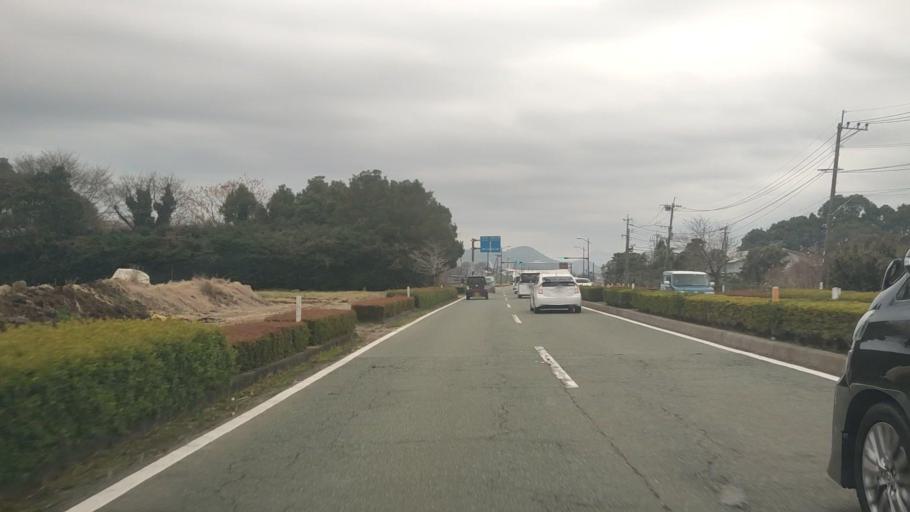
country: JP
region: Kumamoto
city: Ozu
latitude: 32.8435
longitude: 130.8218
